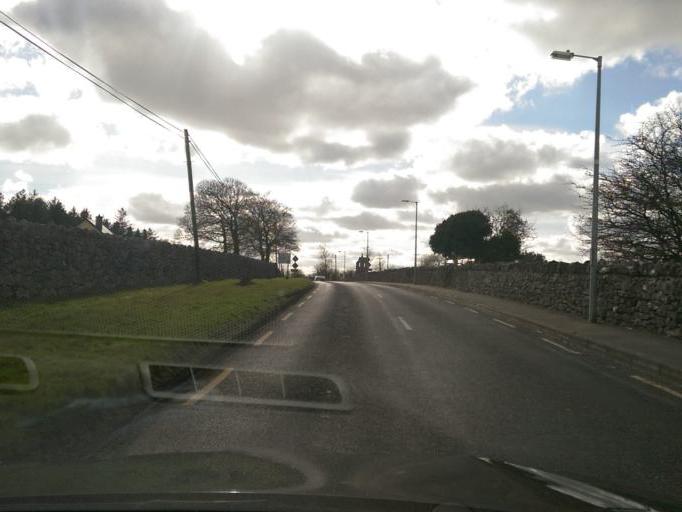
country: IE
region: Connaught
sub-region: County Galway
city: Athenry
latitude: 53.3765
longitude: -8.6987
